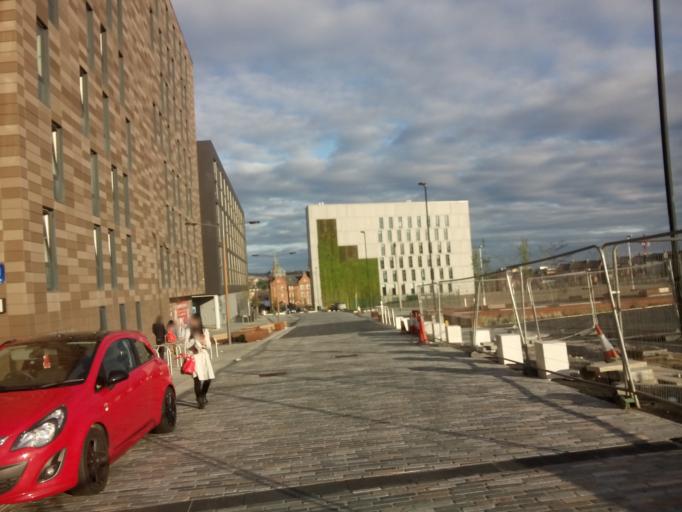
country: GB
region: England
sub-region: Newcastle upon Tyne
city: Newcastle upon Tyne
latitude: 54.9739
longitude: -1.6245
